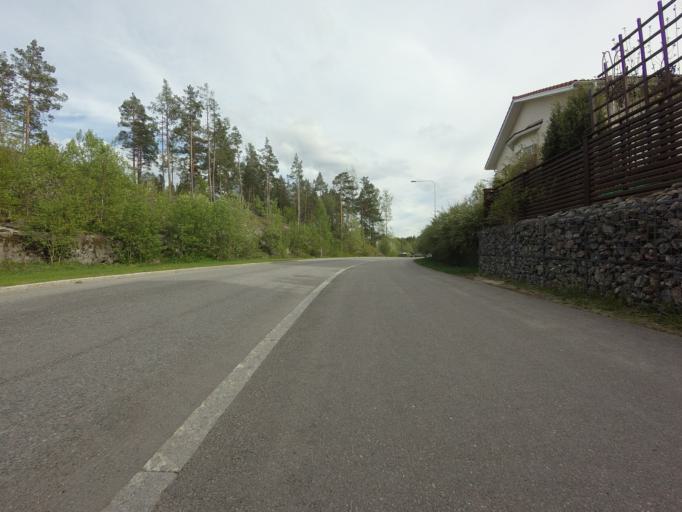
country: FI
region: Uusimaa
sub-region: Helsinki
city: Kauniainen
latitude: 60.1961
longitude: 24.7197
